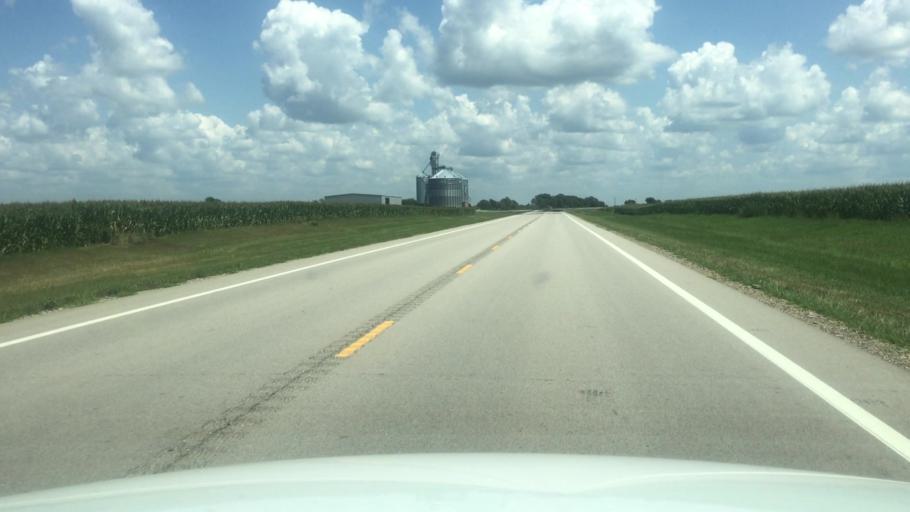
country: US
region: Kansas
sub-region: Brown County
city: Horton
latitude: 39.6603
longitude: -95.3905
